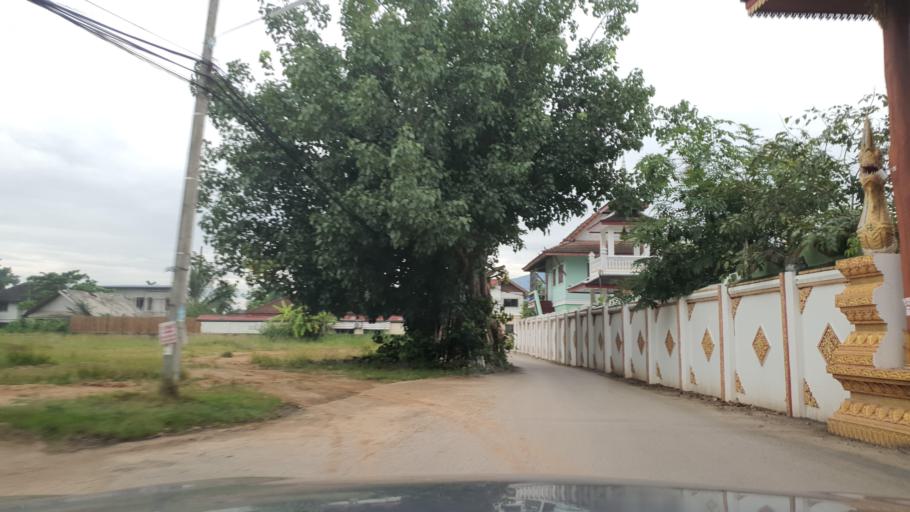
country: TH
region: Chiang Mai
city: San Sai
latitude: 18.9198
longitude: 98.9458
